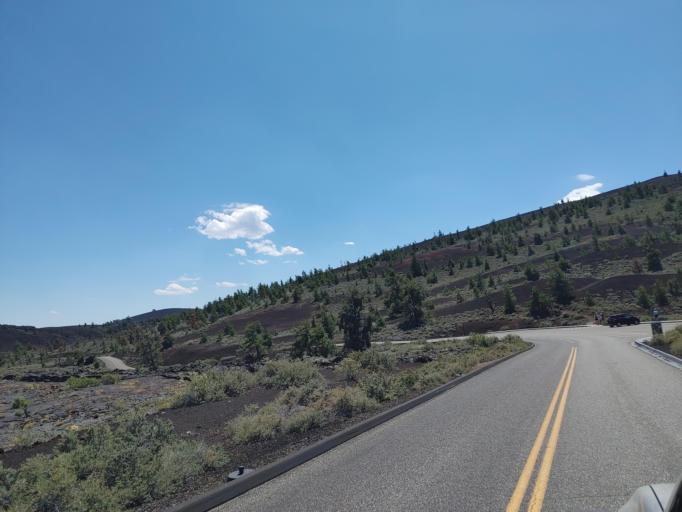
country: US
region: Idaho
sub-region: Butte County
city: Arco
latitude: 43.4568
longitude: -113.5589
